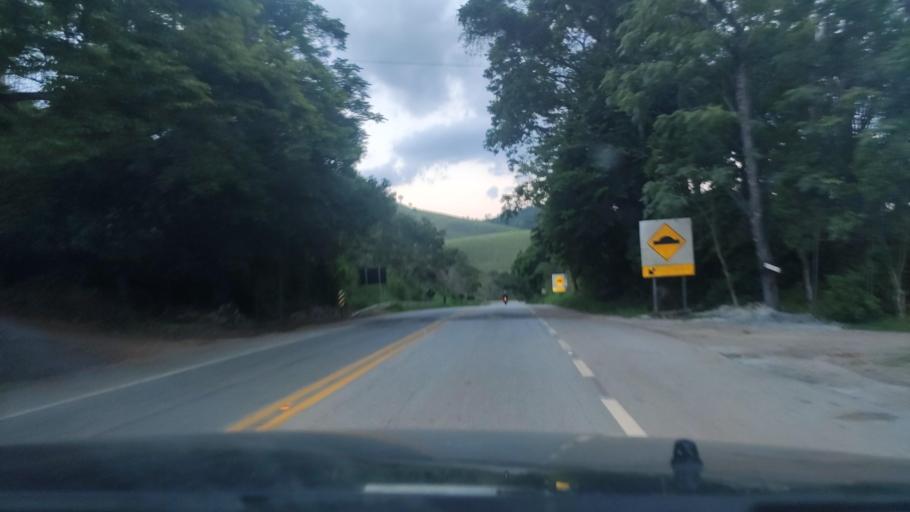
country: BR
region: Sao Paulo
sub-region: Campos Do Jordao
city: Campos do Jordao
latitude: -22.8134
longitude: -45.7531
